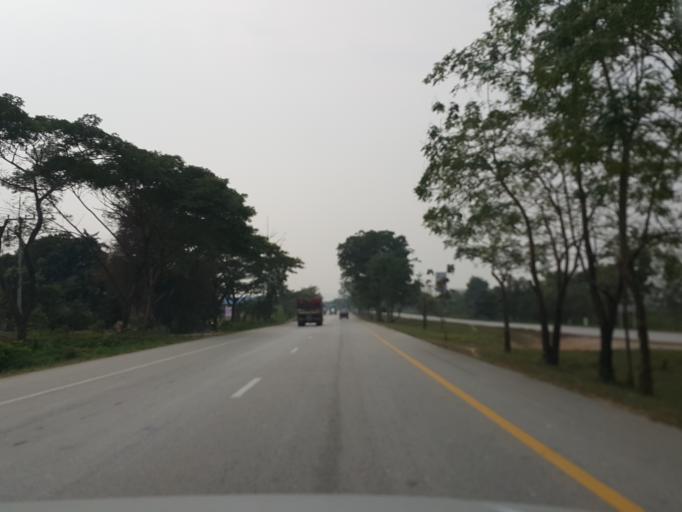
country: TH
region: Lampang
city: Ko Kha
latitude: 18.1625
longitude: 99.4046
